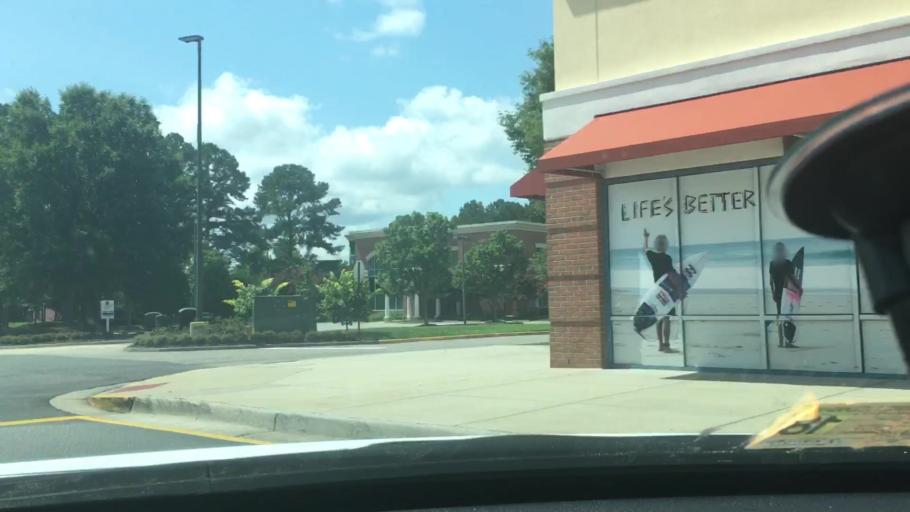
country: US
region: Virginia
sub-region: City of Chesapeake
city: Chesapeake
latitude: 36.7694
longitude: -76.2311
